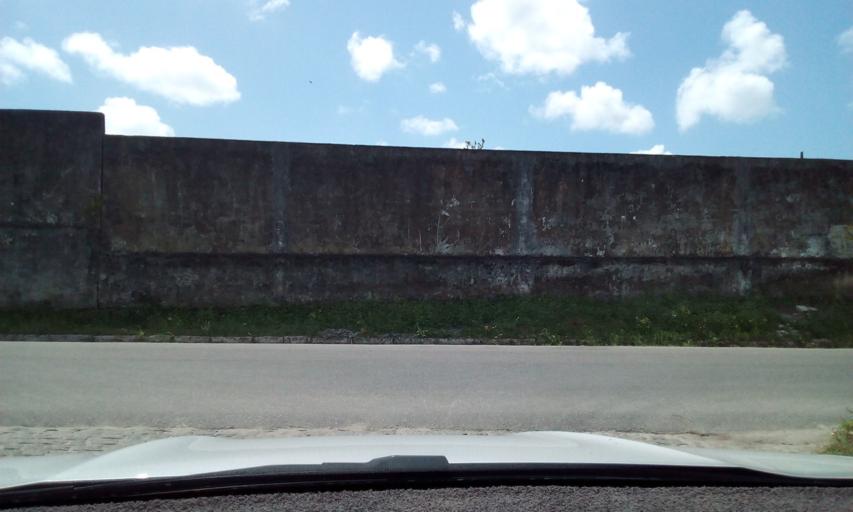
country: BR
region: Paraiba
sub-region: Bayeux
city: Bayeux
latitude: -7.1285
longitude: -34.9263
